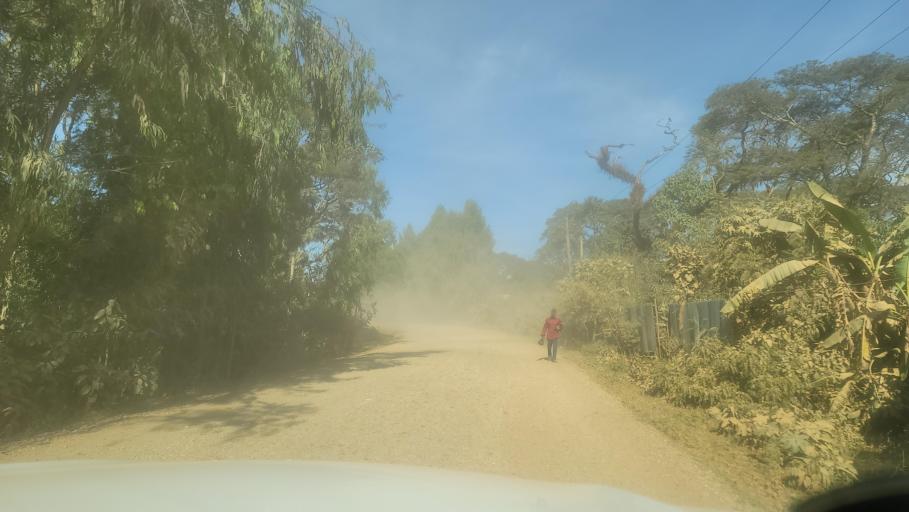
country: ET
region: Oromiya
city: Agaro
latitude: 7.8145
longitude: 36.5103
